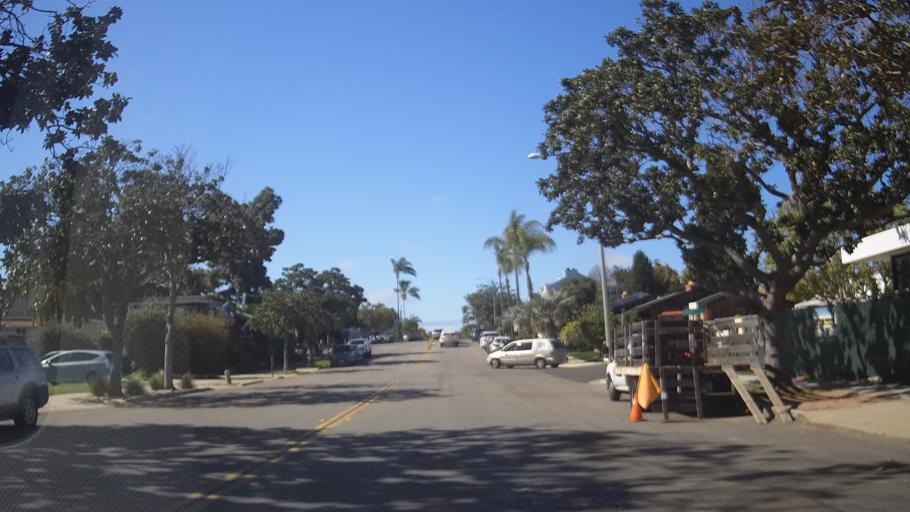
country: US
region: California
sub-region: San Diego County
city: Coronado
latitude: 32.6944
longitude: -117.1702
